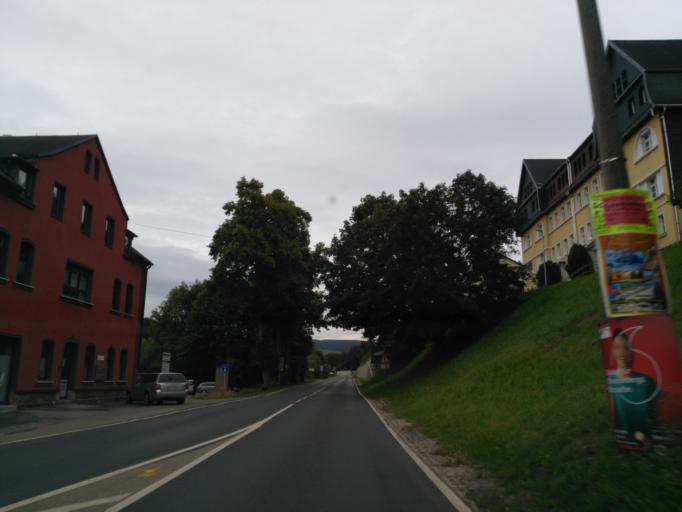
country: DE
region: Saxony
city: Schwarzenberg
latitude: 50.5398
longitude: 12.7962
